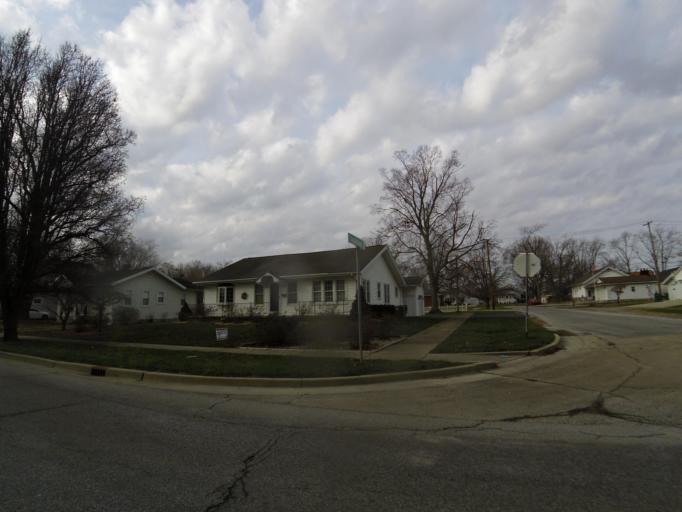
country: US
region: Illinois
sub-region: Christian County
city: Pana
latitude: 39.3789
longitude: -89.0816
